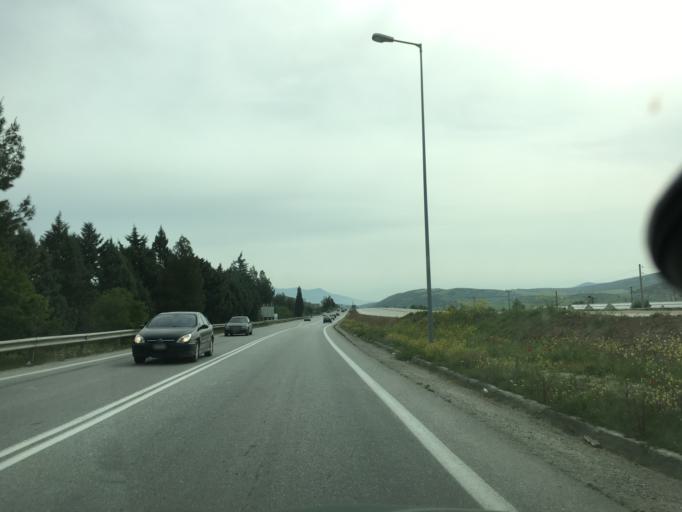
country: GR
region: Thessaly
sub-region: Nomos Magnisias
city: Velestino
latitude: 39.3872
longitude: 22.7828
